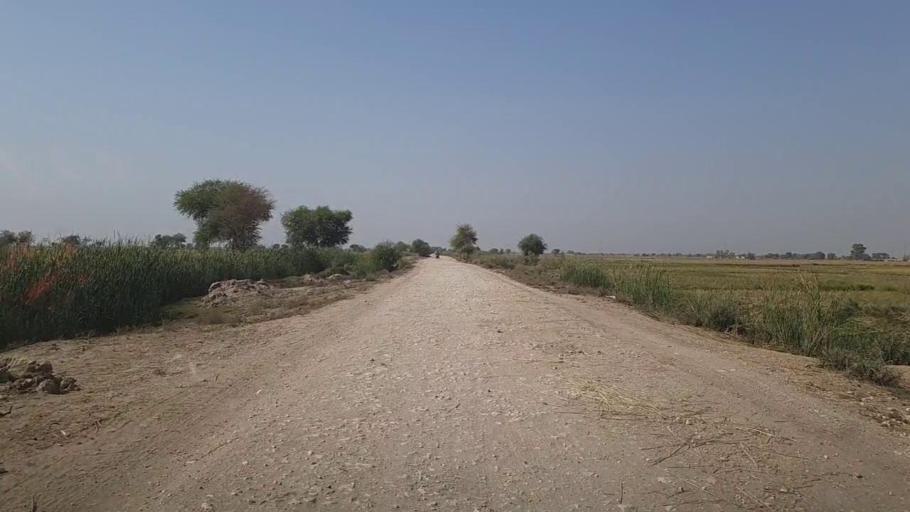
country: PK
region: Sindh
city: Kandhkot
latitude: 28.3985
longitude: 69.2679
